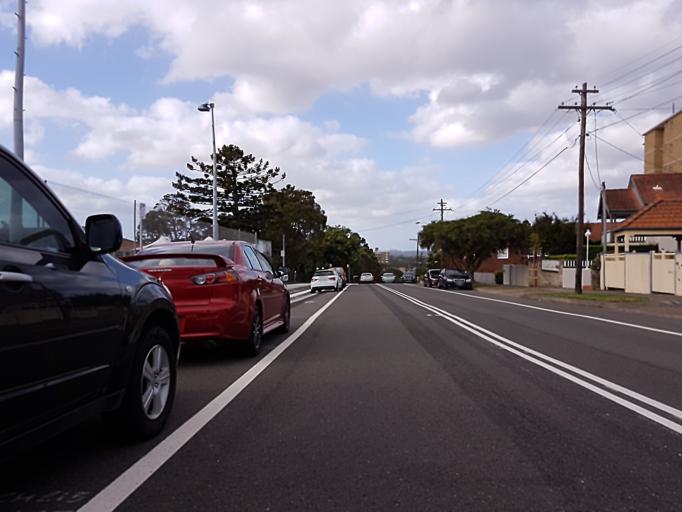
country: AU
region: New South Wales
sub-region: North Sydney
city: Cammeray
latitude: -33.8277
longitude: 151.2174
